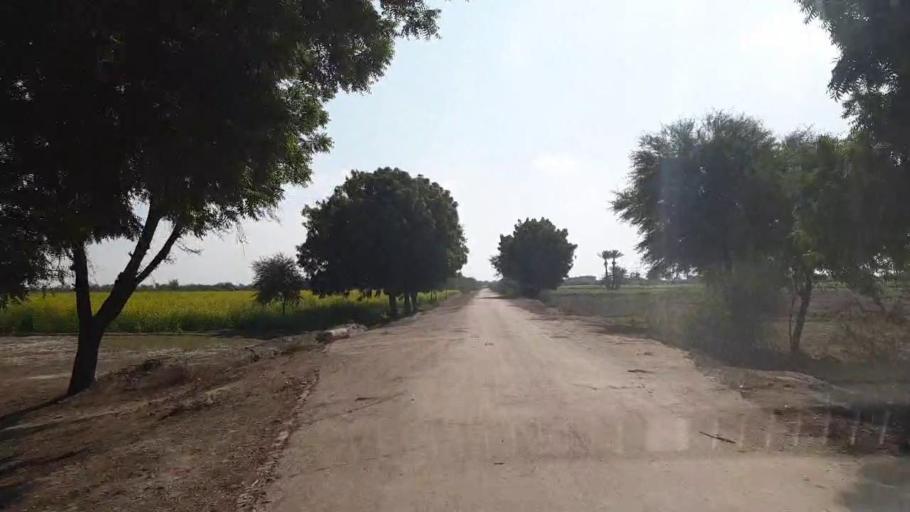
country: PK
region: Sindh
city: Shahpur Chakar
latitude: 26.0504
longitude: 68.6058
